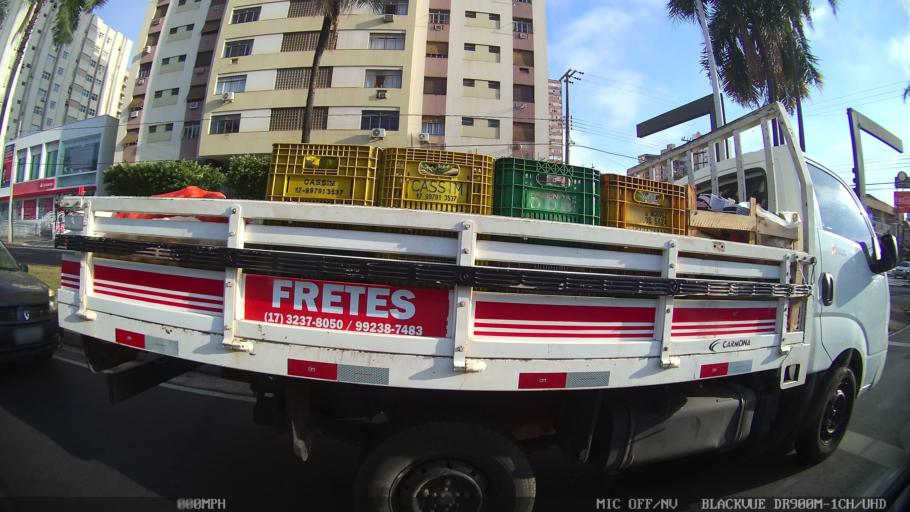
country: BR
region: Sao Paulo
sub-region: Sao Jose Do Rio Preto
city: Sao Jose do Rio Preto
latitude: -20.8152
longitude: -49.3796
